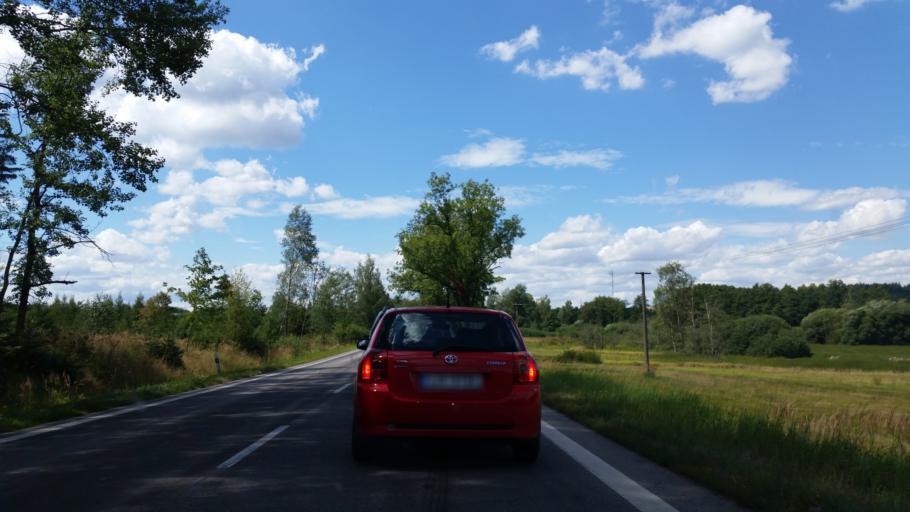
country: CZ
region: Vysocina
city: Cernovice
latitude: 49.4226
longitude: 14.9622
